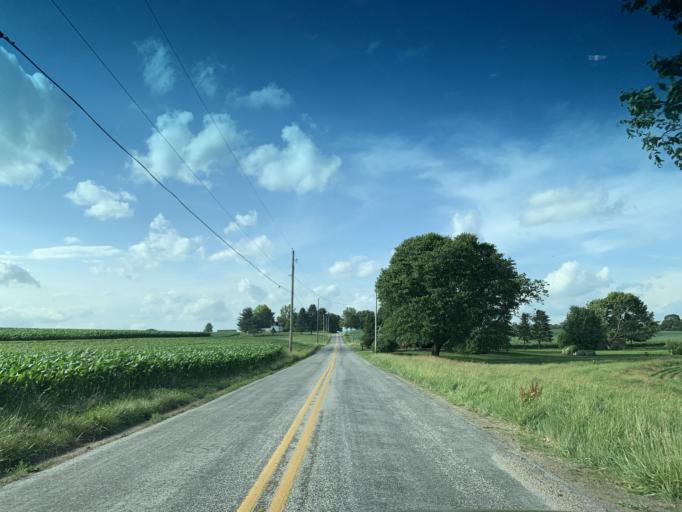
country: US
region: Pennsylvania
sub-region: York County
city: Stewartstown
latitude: 39.7242
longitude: -76.5433
